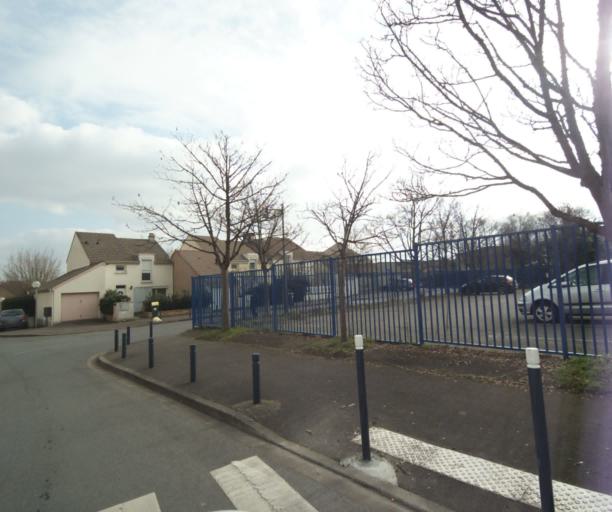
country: FR
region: Ile-de-France
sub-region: Departement du Val-d'Oise
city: Vaureal
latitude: 49.0460
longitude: 2.0439
